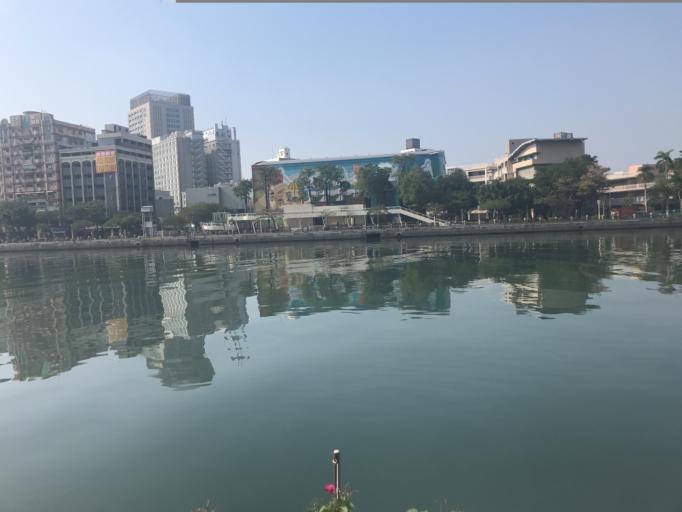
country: TW
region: Kaohsiung
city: Kaohsiung
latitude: 22.6234
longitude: 120.2903
